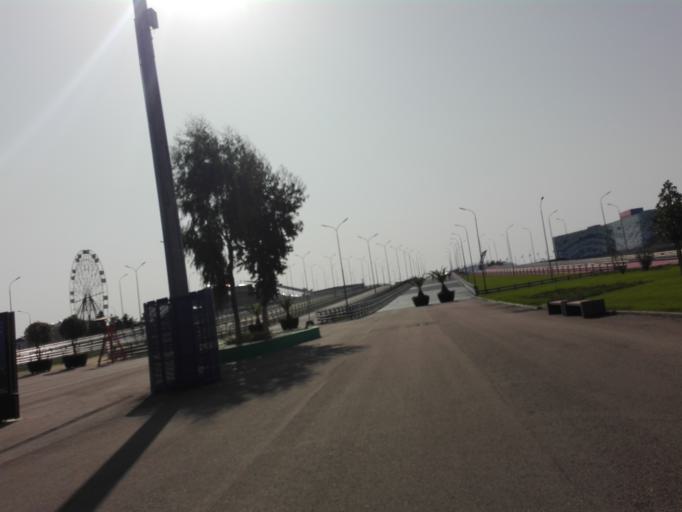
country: RU
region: Krasnodarskiy
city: Adler
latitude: 43.4069
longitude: 39.9652
